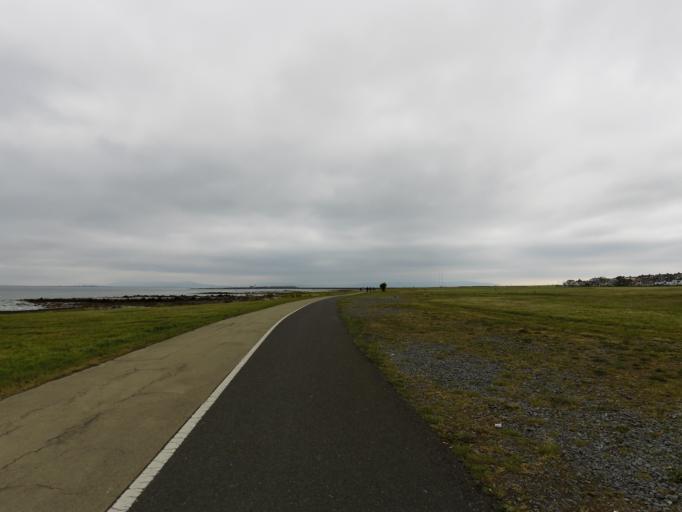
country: IE
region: Connaught
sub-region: County Galway
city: Gaillimh
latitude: 53.2663
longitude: -9.0503
